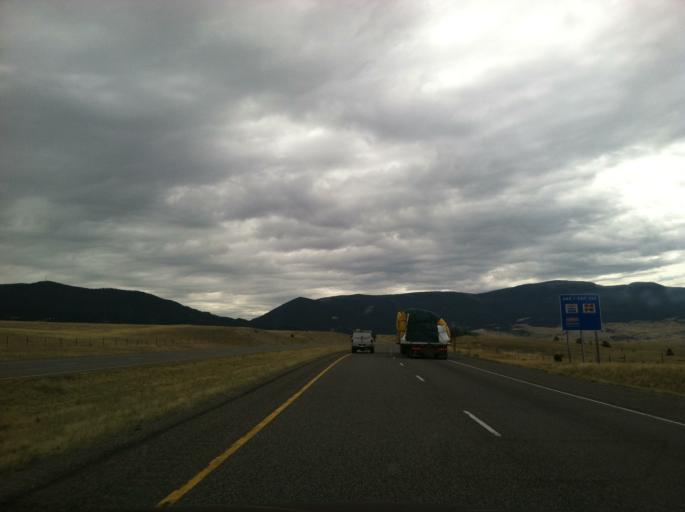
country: US
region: Montana
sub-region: Park County
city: Livingston
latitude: 45.6560
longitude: -110.5369
